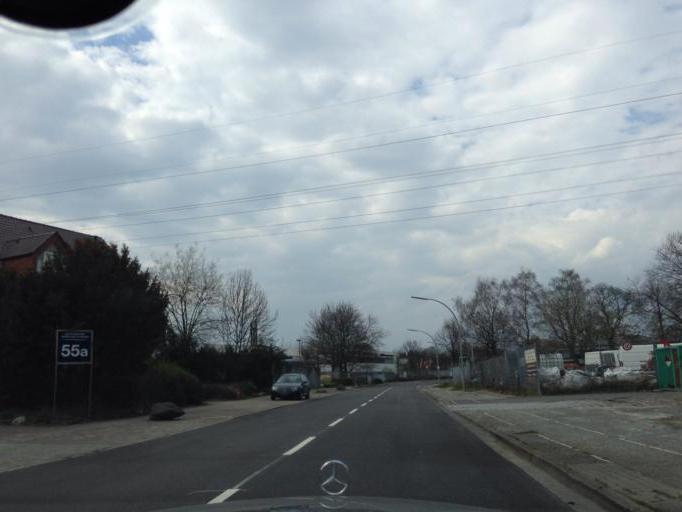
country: DE
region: Hamburg
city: Wandsbek
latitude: 53.5767
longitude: 10.1119
